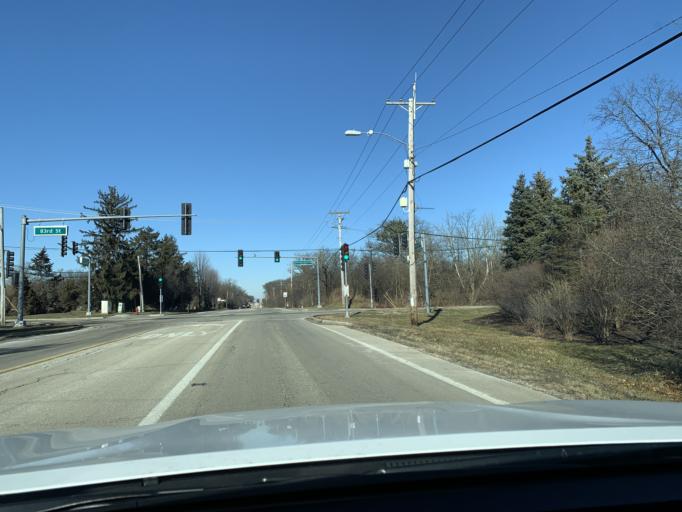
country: US
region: Illinois
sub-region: DuPage County
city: Burr Ridge
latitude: 41.7381
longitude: -87.9151
